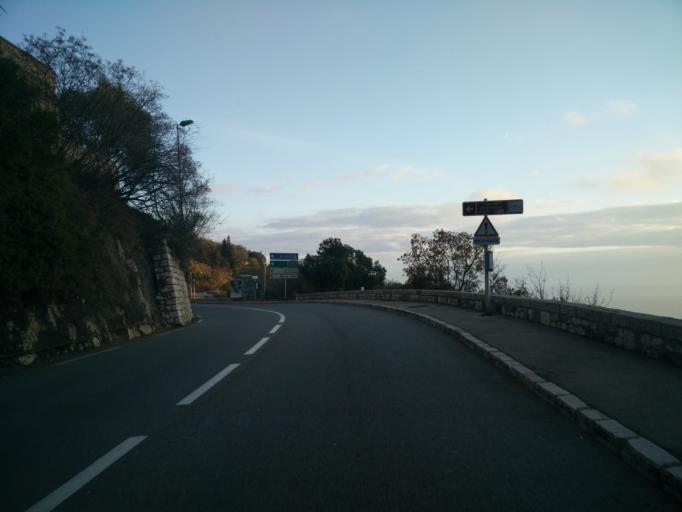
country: FR
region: Provence-Alpes-Cote d'Azur
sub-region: Departement des Alpes-Maritimes
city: Eze
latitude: 43.7307
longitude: 7.3653
